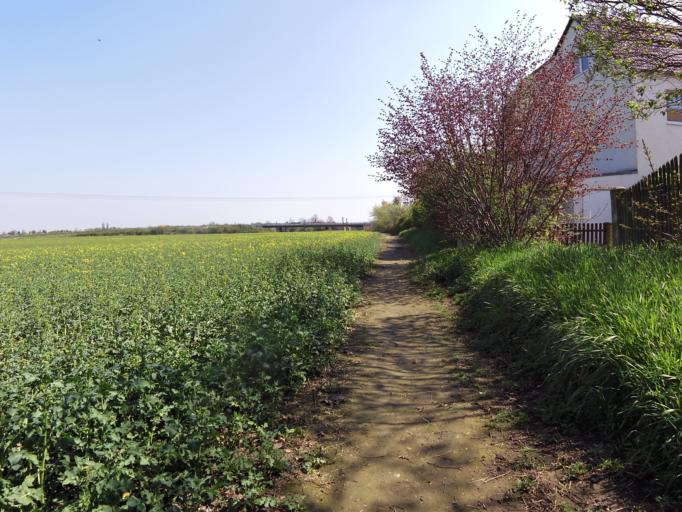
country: DE
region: Saxony
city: Leipzig
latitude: 51.3815
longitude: 12.3367
